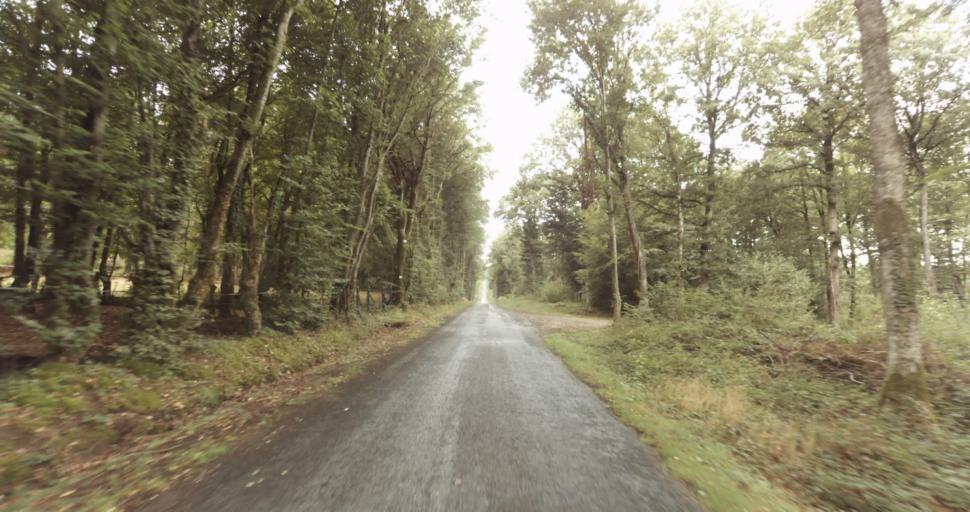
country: FR
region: Lower Normandy
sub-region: Departement de l'Orne
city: Sainte-Gauburge-Sainte-Colombe
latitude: 48.7542
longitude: 0.4858
